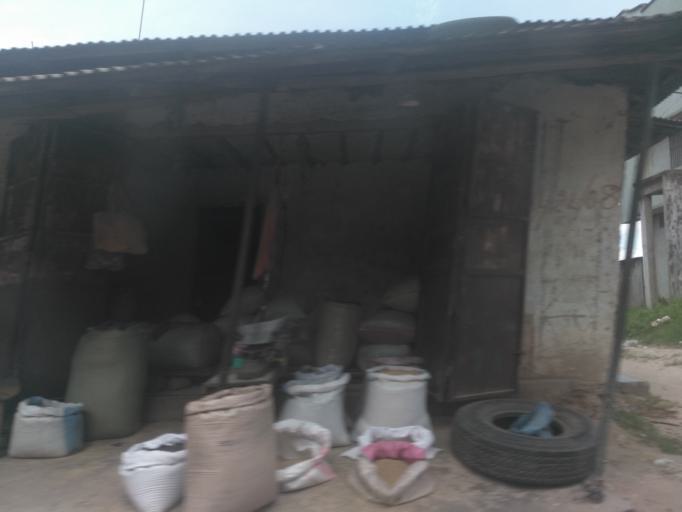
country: TZ
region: Zanzibar Urban/West
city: Zanzibar
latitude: -6.1542
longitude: 39.2075
